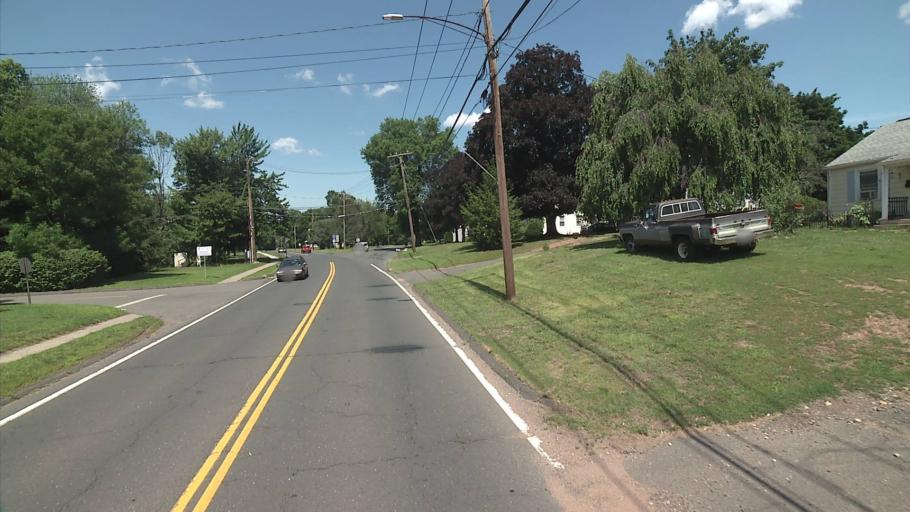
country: US
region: Connecticut
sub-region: Middlesex County
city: Cromwell
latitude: 41.6042
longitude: -72.6609
